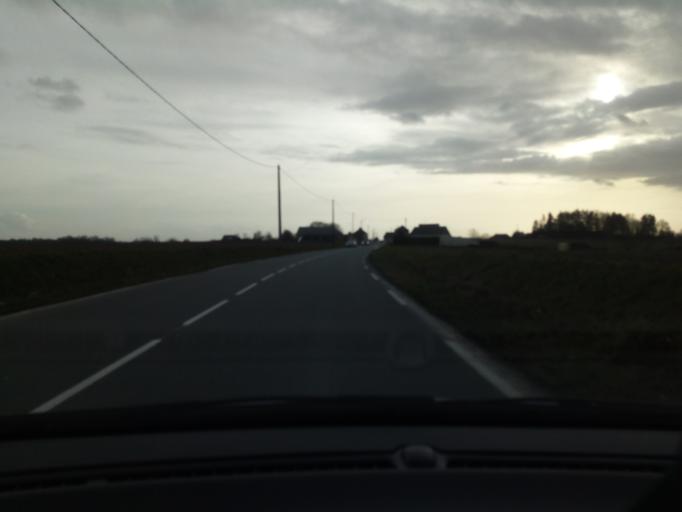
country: FR
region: Nord-Pas-de-Calais
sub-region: Departement du Nord
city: La Longueville
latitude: 50.3291
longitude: 3.8679
